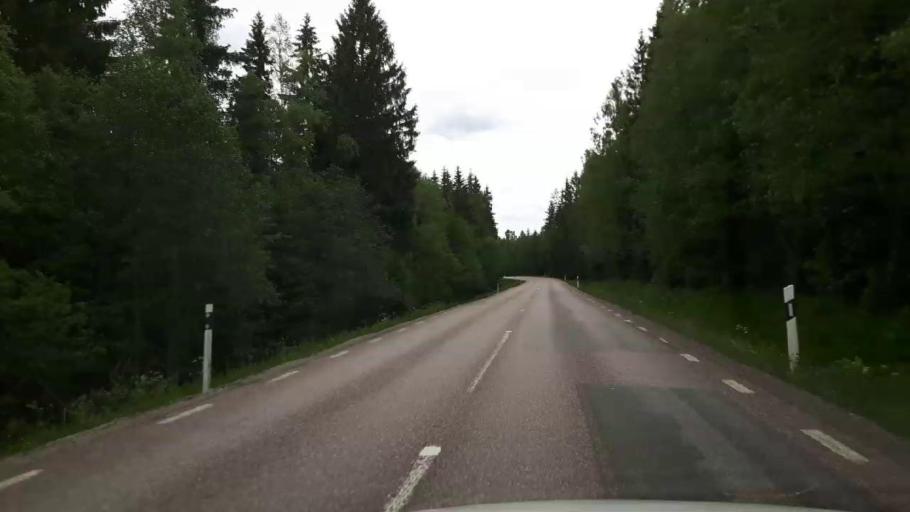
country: SE
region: Dalarna
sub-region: Hedemora Kommun
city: Brunna
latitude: 60.1821
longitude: 15.9990
